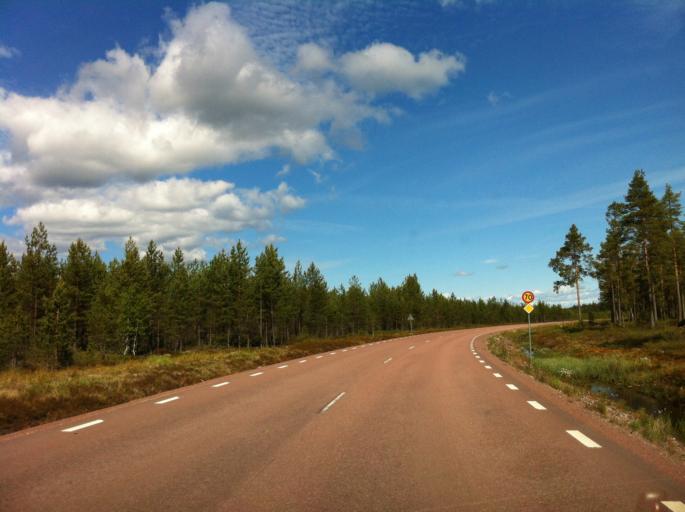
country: SE
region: Dalarna
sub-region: Mora Kommun
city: Mora
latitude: 60.9684
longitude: 14.5087
